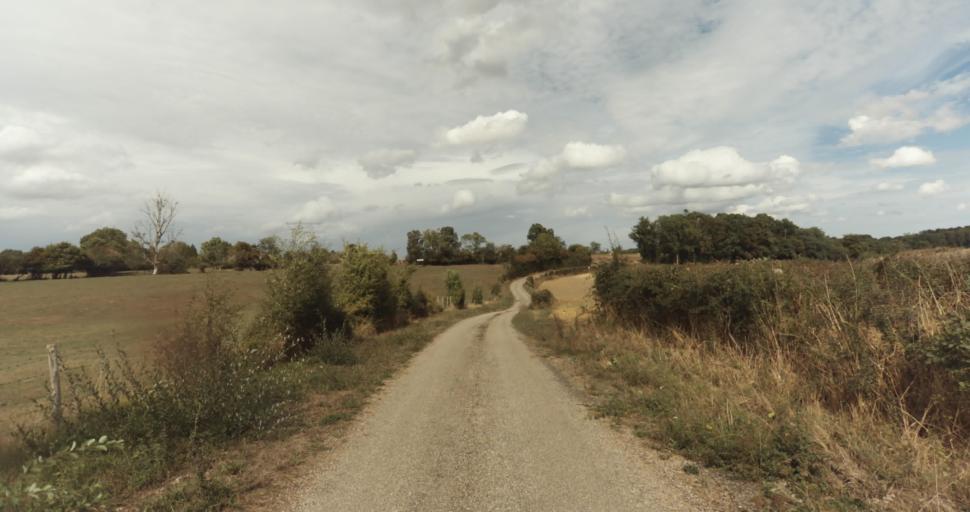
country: FR
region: Lower Normandy
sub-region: Departement du Calvados
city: Orbec
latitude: 48.9104
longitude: 0.3768
